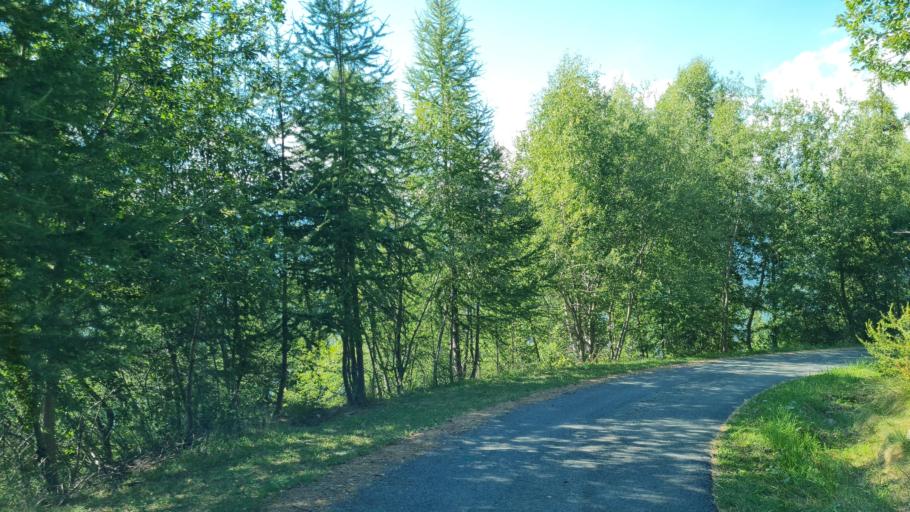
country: IT
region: Aosta Valley
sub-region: Valle d'Aosta
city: Fontainemore
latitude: 45.6276
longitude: 7.8711
